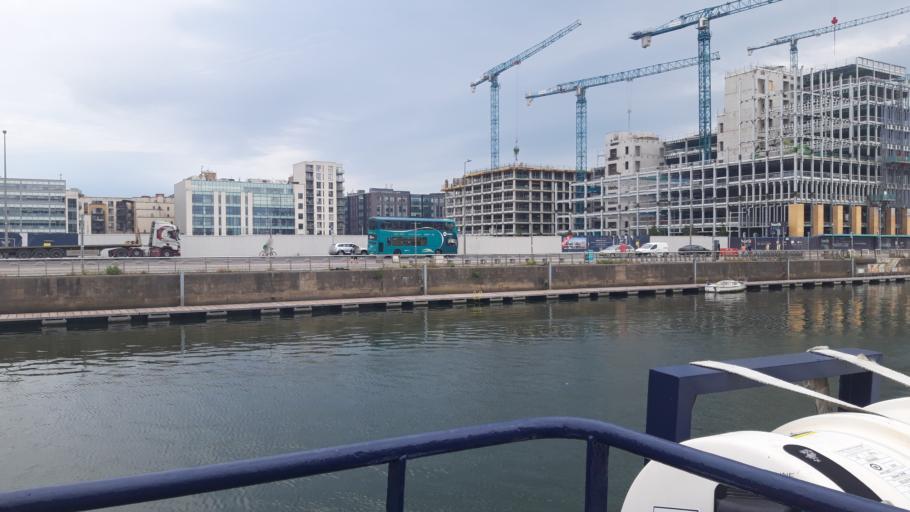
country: IE
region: Leinster
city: Ringsend
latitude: 53.3464
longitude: -6.2319
